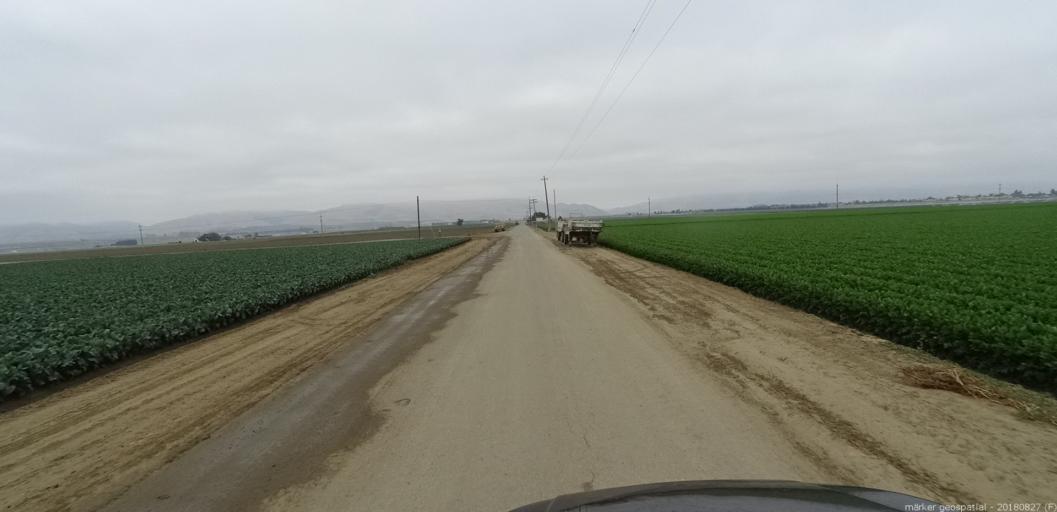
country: US
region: California
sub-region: Monterey County
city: Greenfield
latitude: 36.3195
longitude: -121.2098
